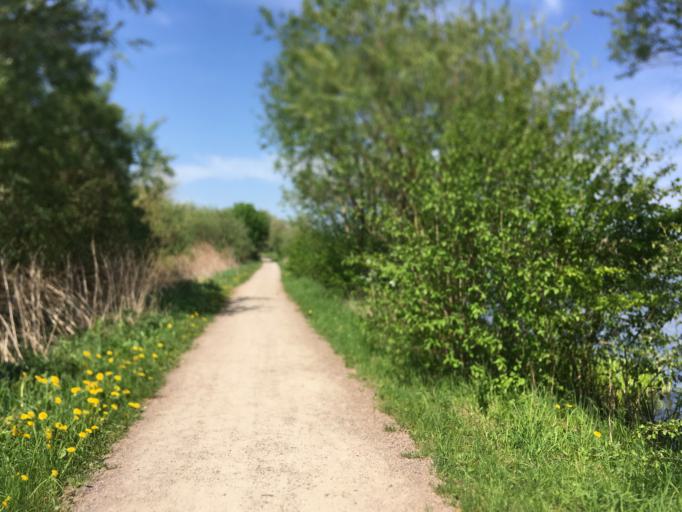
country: SE
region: Skane
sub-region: Staffanstorps Kommun
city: Hjaerup
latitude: 55.6966
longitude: 13.1571
